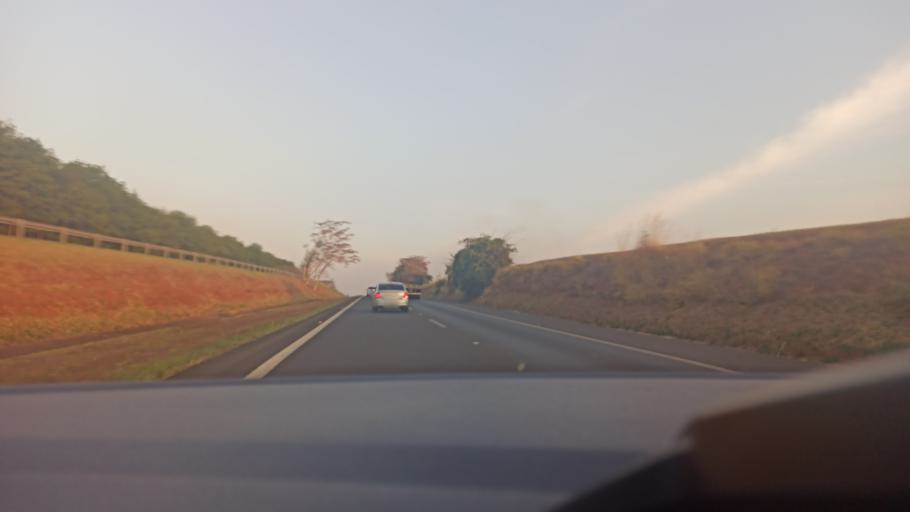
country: BR
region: Sao Paulo
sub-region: Taquaritinga
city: Taquaritinga
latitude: -21.4528
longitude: -48.6316
